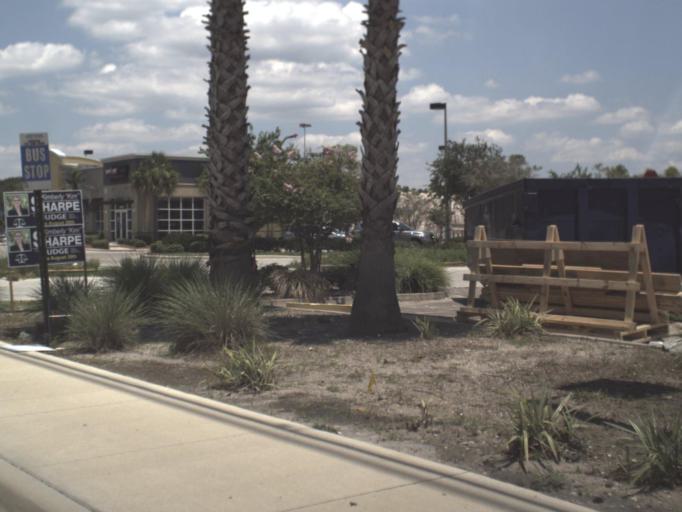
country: US
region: Florida
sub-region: Pinellas County
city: South Highpoint
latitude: 27.9397
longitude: -82.7300
